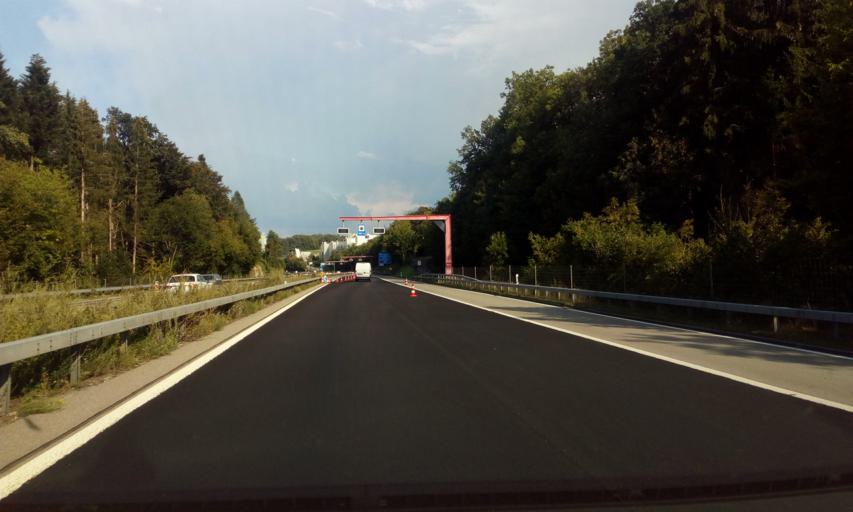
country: CH
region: Bern
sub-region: Bern-Mittelland District
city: Frauenkappelen
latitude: 46.9449
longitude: 7.3608
